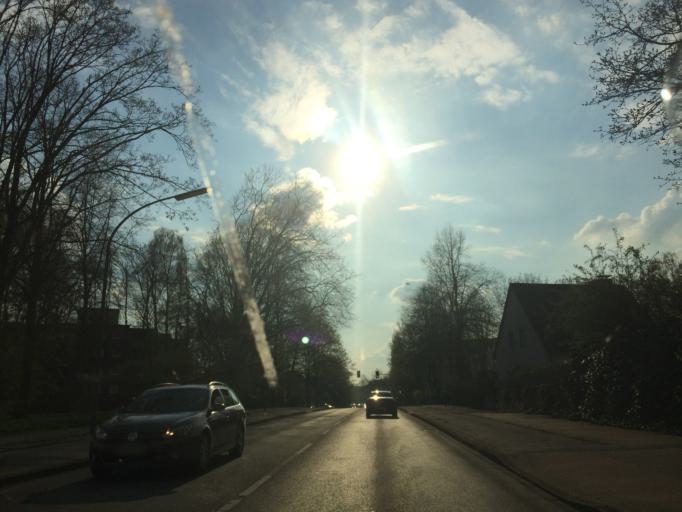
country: DE
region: North Rhine-Westphalia
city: Herten
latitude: 51.5704
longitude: 7.0850
